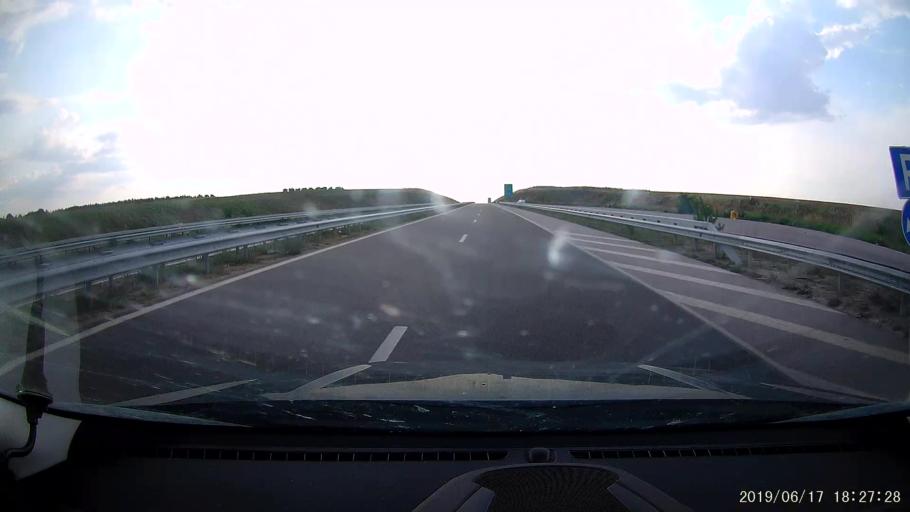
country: BG
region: Khaskovo
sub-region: Obshtina Dimitrovgrad
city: Dimitrovgrad
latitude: 42.0170
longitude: 25.6078
